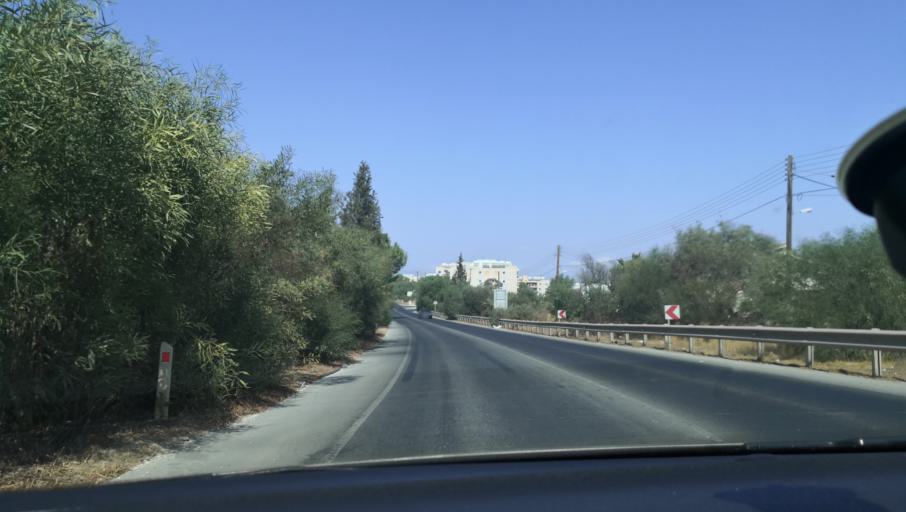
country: CY
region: Lefkosia
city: Kato Deftera
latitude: 35.0994
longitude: 33.2871
